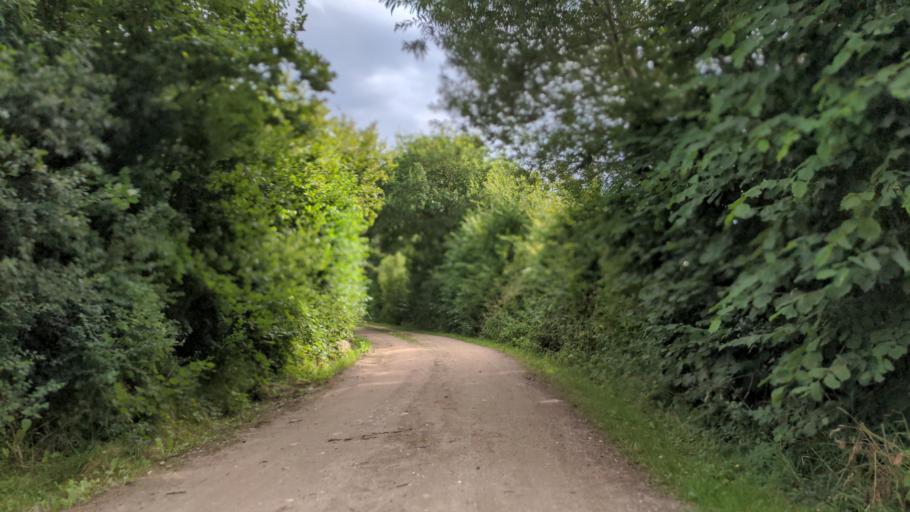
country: DE
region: Schleswig-Holstein
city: Dahme
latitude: 54.2010
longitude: 11.0852
